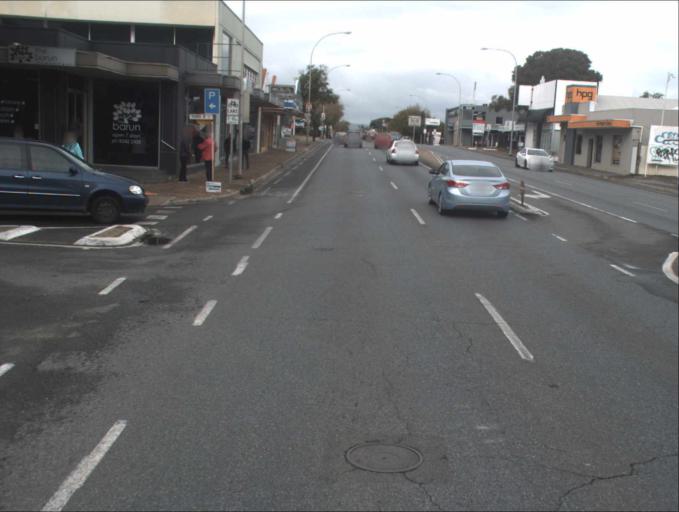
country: AU
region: South Australia
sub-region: Prospect
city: Prospect
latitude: -34.8777
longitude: 138.6023
